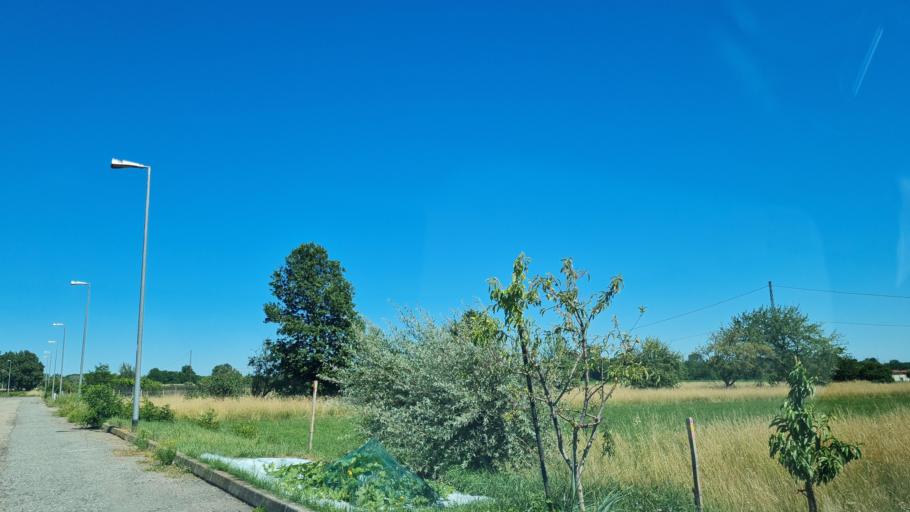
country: IT
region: Piedmont
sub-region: Provincia di Biella
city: Occhieppo Inferiore
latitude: 45.5445
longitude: 8.0256
